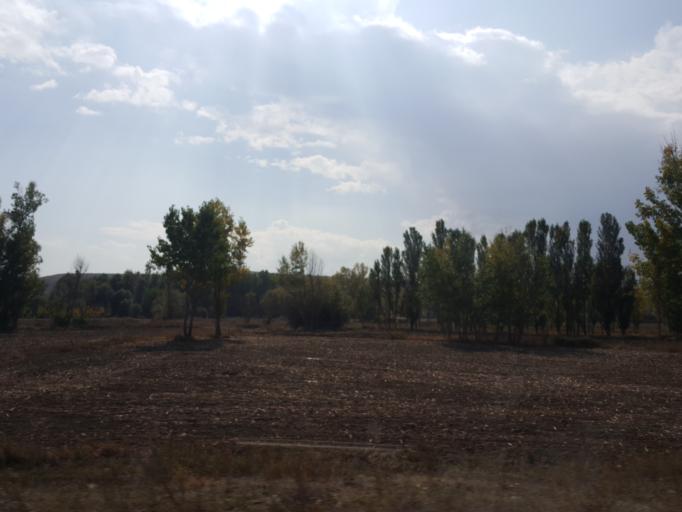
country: TR
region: Corum
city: Alaca
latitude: 40.1393
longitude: 34.8123
